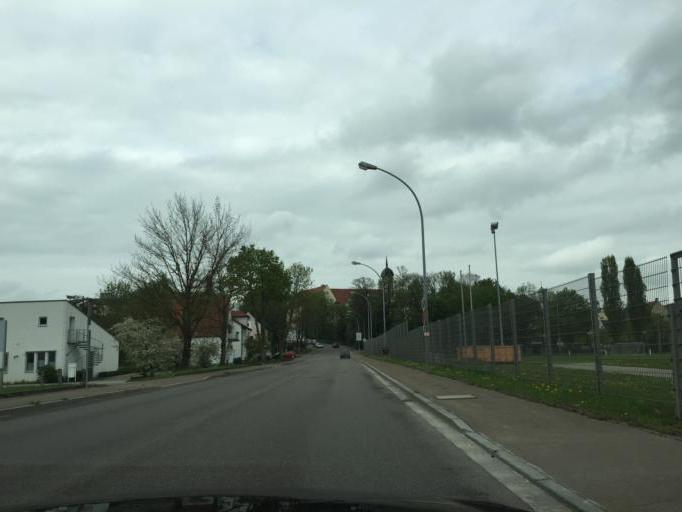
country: DE
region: Bavaria
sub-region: Swabia
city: Dillingen an der Donau
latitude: 48.5737
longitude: 10.4892
